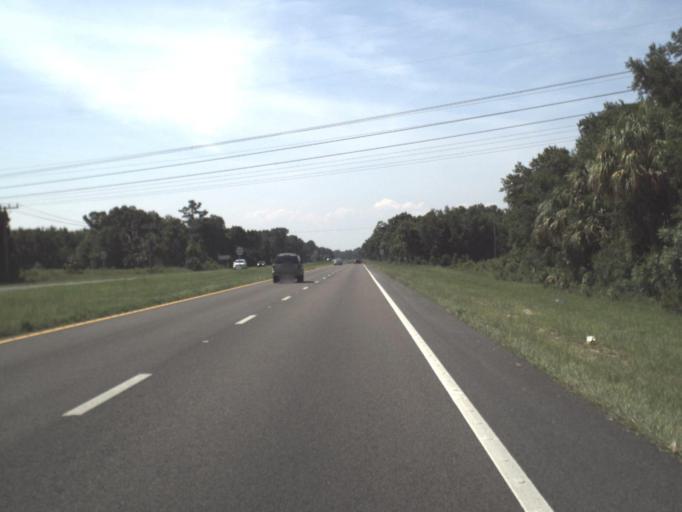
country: US
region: Florida
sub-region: Citrus County
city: Crystal River
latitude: 28.9602
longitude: -82.6305
